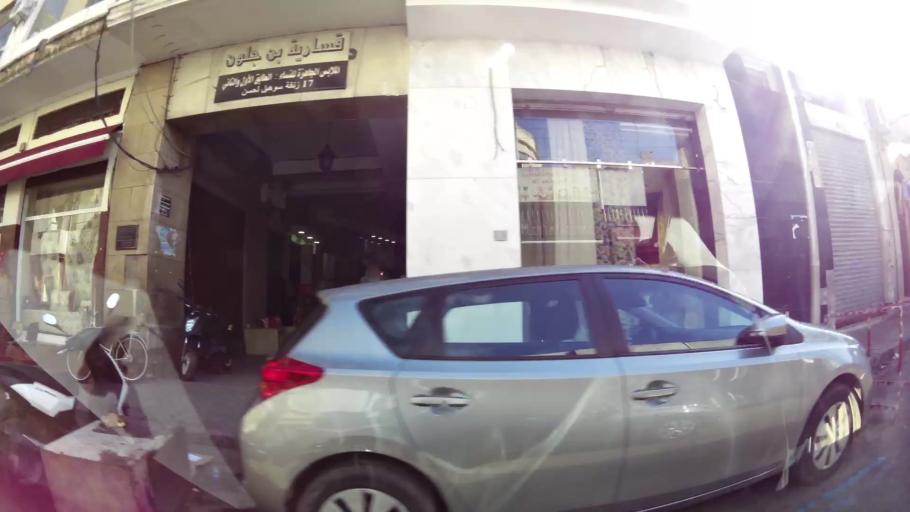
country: MA
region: Grand Casablanca
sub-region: Casablanca
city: Casablanca
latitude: 33.5911
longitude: -7.6120
